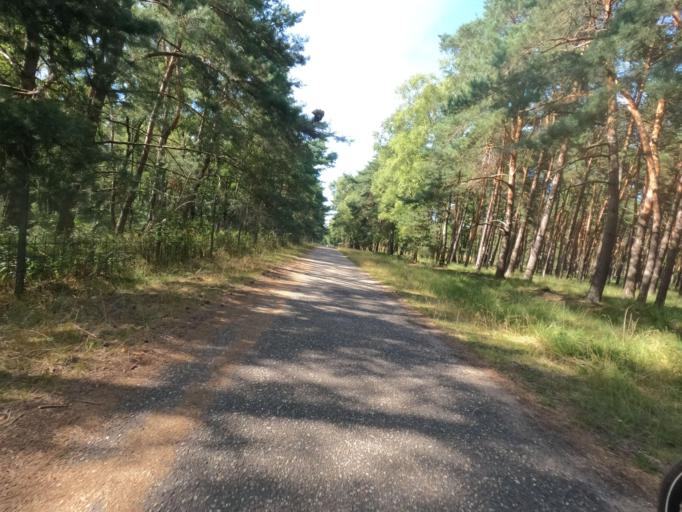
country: NL
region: Limburg
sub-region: Gemeente Beesel
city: Offenbeek
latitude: 51.2708
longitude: 6.1375
